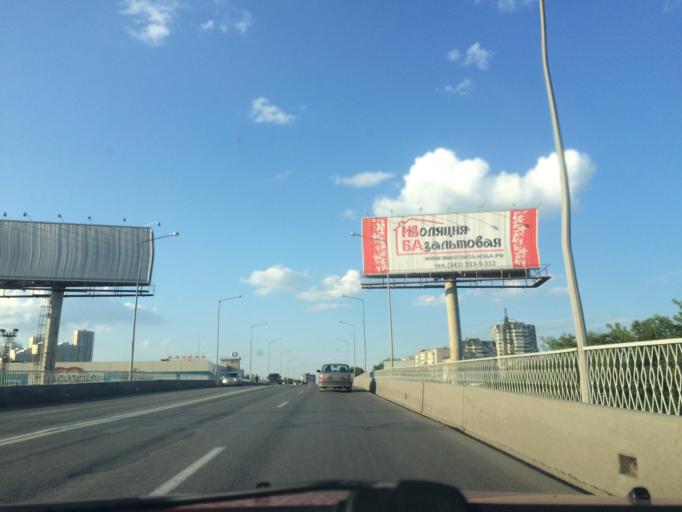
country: RU
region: Sverdlovsk
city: Yekaterinburg
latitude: 56.8251
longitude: 60.6591
